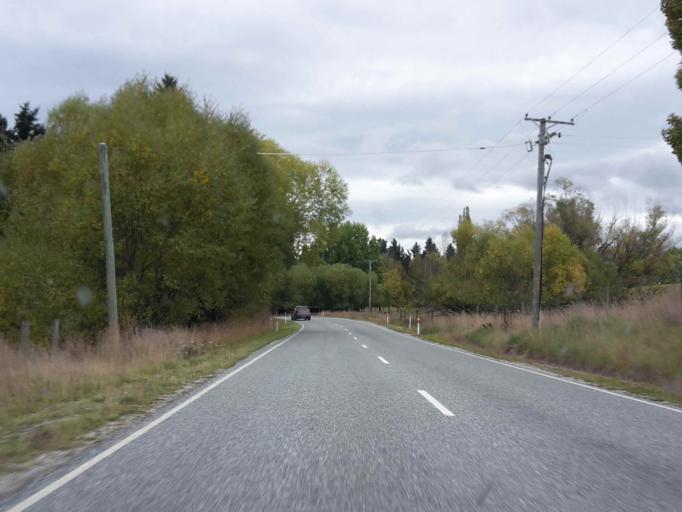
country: NZ
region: Otago
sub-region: Queenstown-Lakes District
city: Arrowtown
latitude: -44.9763
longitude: 168.8696
